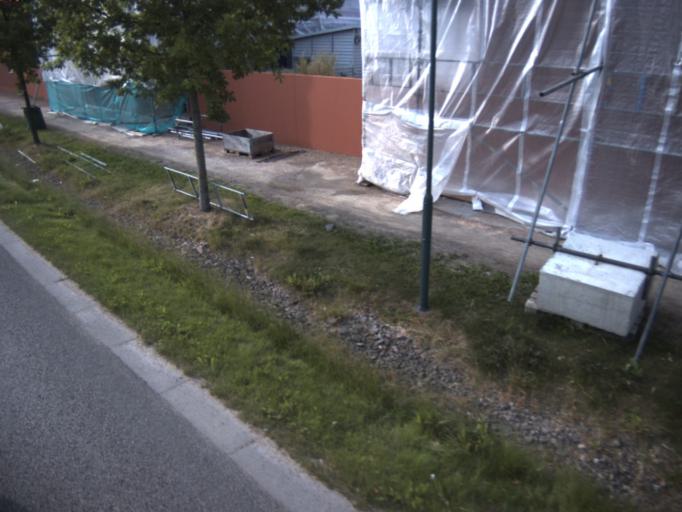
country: SE
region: Skane
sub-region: Helsingborg
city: Helsingborg
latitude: 56.0818
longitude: 12.6946
